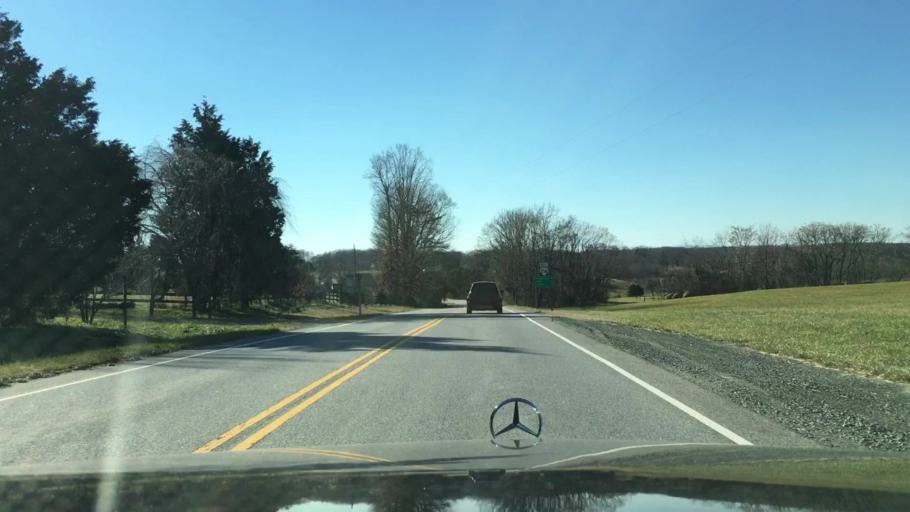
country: US
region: Virginia
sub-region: City of Bedford
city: Bedford
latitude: 37.2231
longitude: -79.4694
